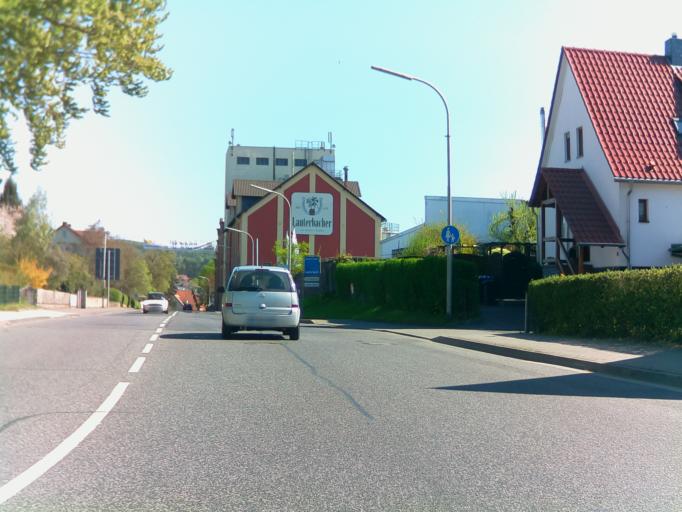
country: DE
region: Hesse
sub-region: Regierungsbezirk Giessen
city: Lauterbach
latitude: 50.6410
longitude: 9.3917
